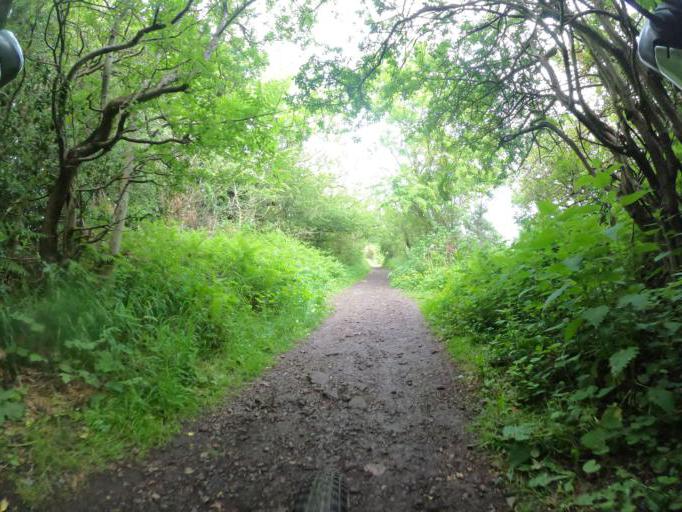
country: GB
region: Scotland
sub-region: Edinburgh
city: Currie
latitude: 55.9064
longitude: -3.3031
